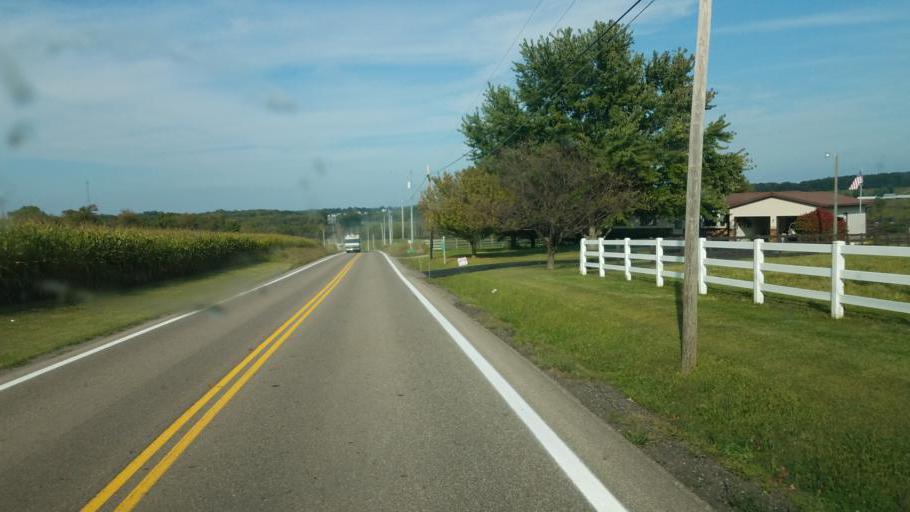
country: US
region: Ohio
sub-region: Knox County
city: Gambier
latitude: 40.2789
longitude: -82.3494
